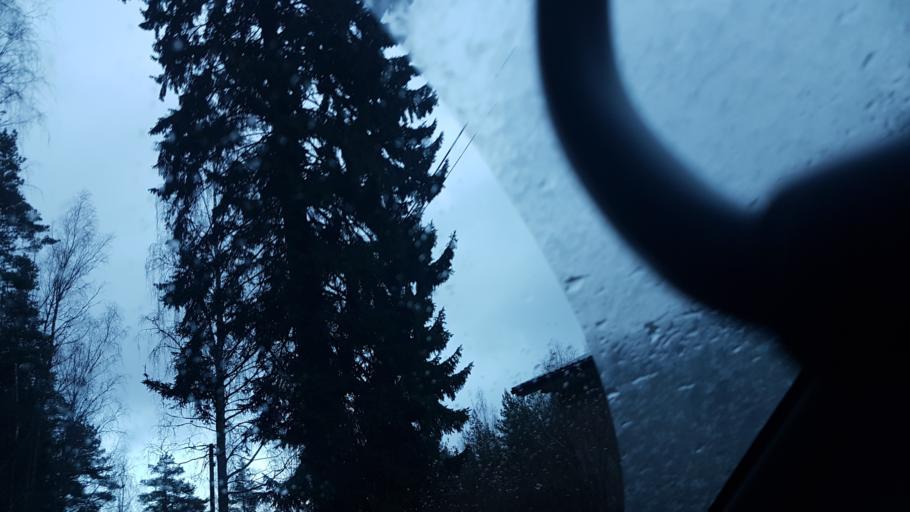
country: FI
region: Uusimaa
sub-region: Helsinki
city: Lohja
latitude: 60.2139
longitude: 24.0901
